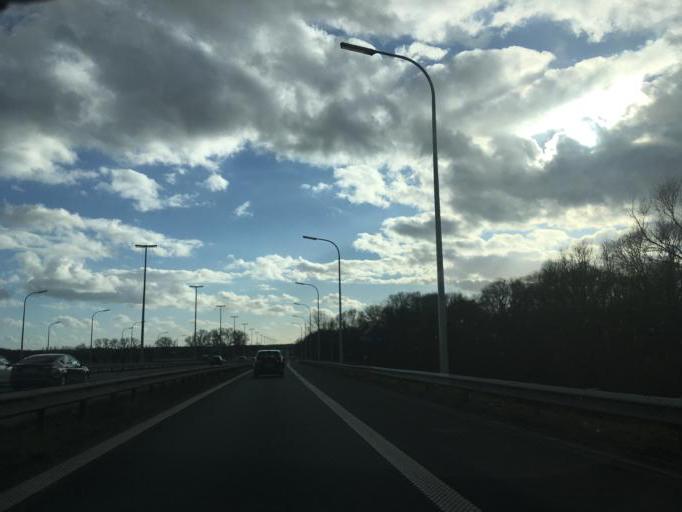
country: BE
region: Flanders
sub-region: Provincie West-Vlaanderen
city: Oostkamp
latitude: 51.1542
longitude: 3.2111
